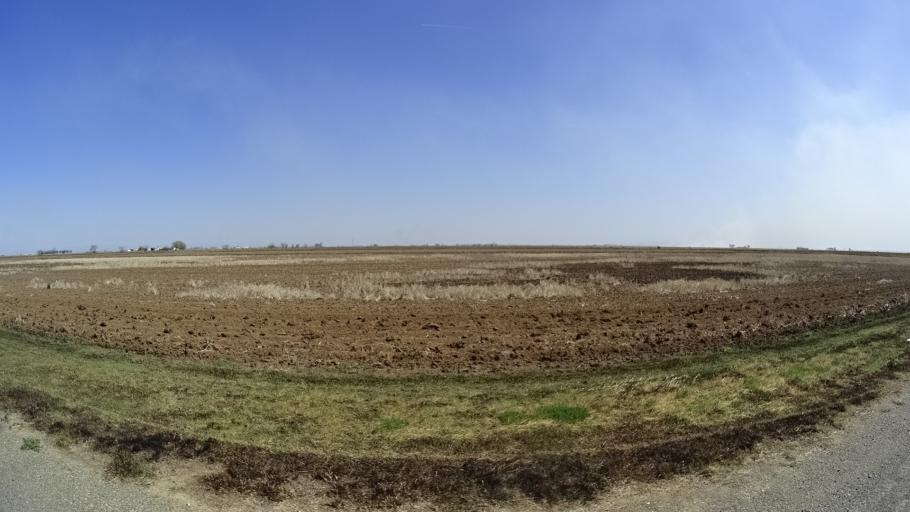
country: US
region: California
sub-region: Glenn County
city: Willows
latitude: 39.4013
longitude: -122.2483
